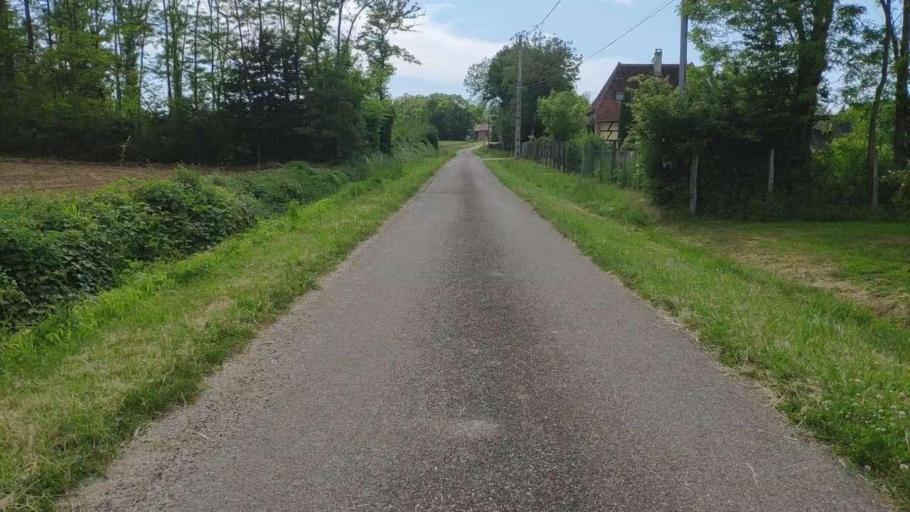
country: FR
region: Franche-Comte
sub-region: Departement du Jura
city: Petit-Noir
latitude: 46.8177
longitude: 5.3566
